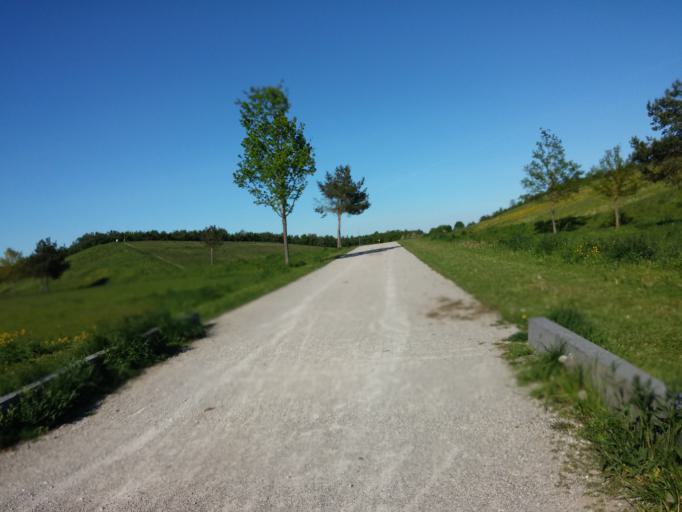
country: DE
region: Bavaria
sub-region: Upper Bavaria
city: Feldkirchen
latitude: 48.1314
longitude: 11.7088
